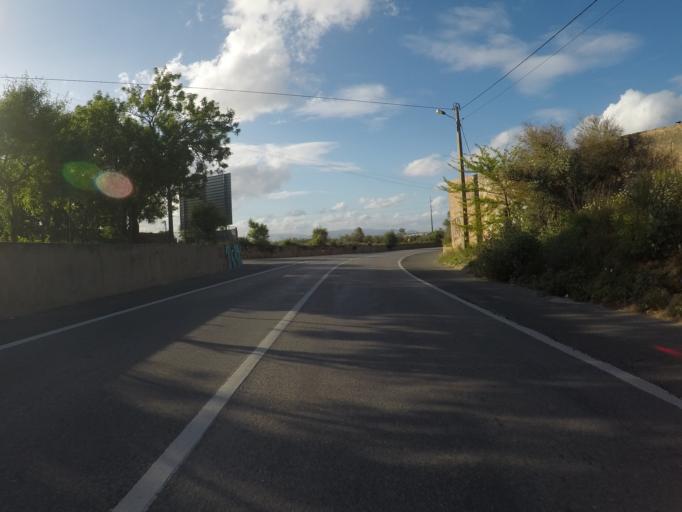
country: PT
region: Faro
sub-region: Lagoa
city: Lagoa
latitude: 37.1169
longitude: -8.4558
